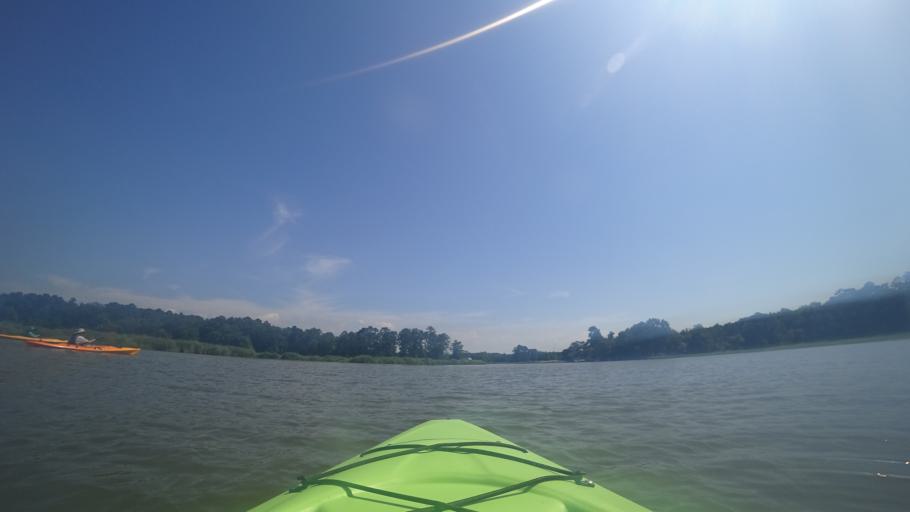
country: US
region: Virginia
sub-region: Isle of Wight County
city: Smithfield
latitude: 36.9572
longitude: -76.6162
